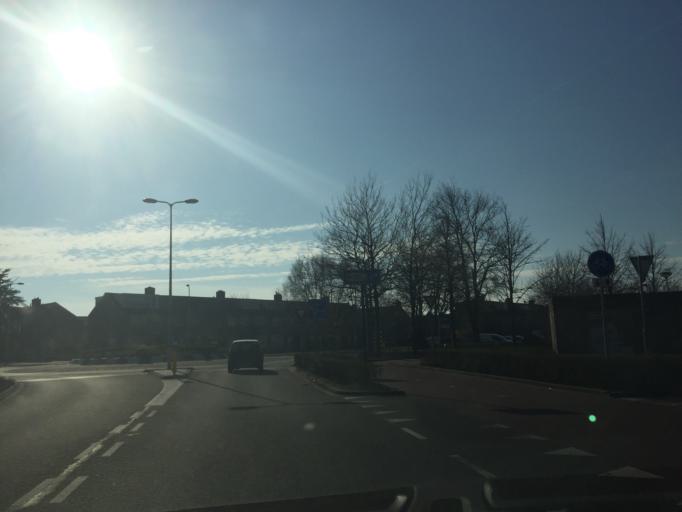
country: NL
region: South Holland
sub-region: Gemeente Noordwijkerhout
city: Noordwijkerhout
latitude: 52.2572
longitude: 4.5003
